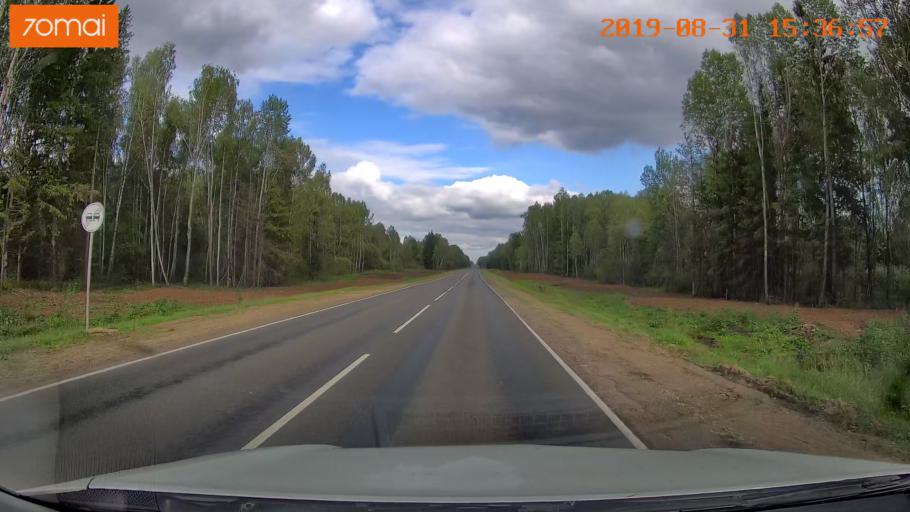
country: RU
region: Kaluga
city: Mosal'sk
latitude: 54.6149
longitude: 34.7723
